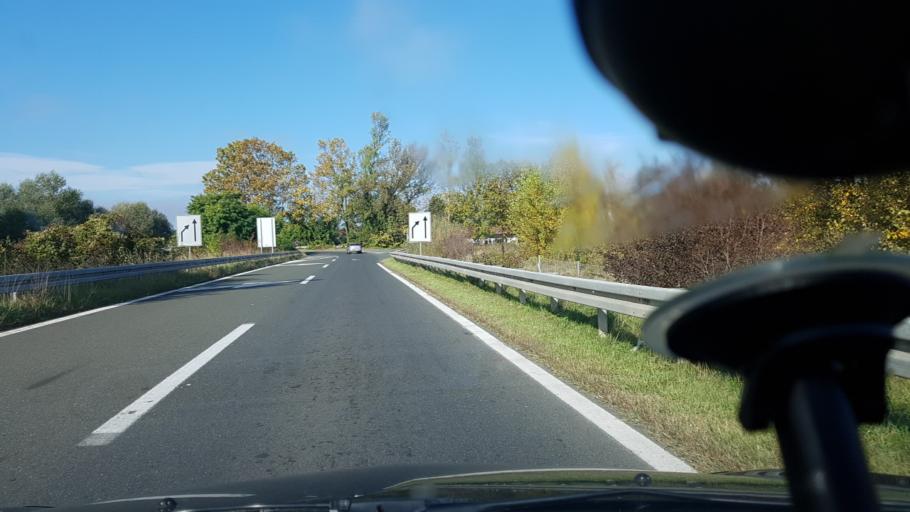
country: HR
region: Zagrebacka
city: Rakitje
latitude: 45.7855
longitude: 15.8315
